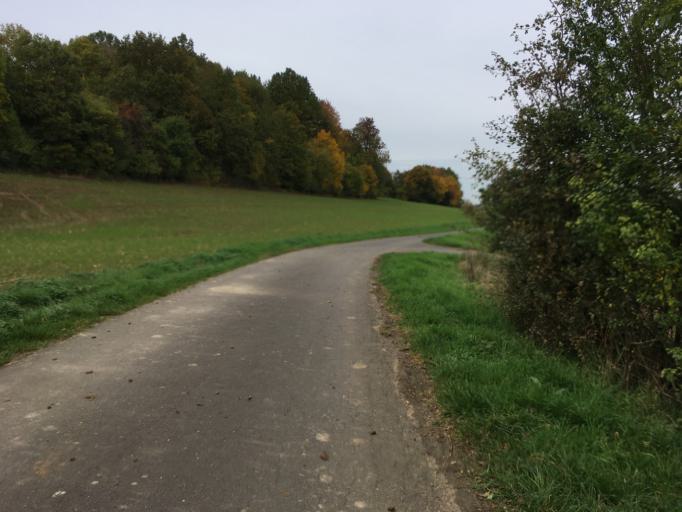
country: DE
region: Baden-Wuerttemberg
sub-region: Karlsruhe Region
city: Seckach
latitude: 49.4484
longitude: 9.3307
